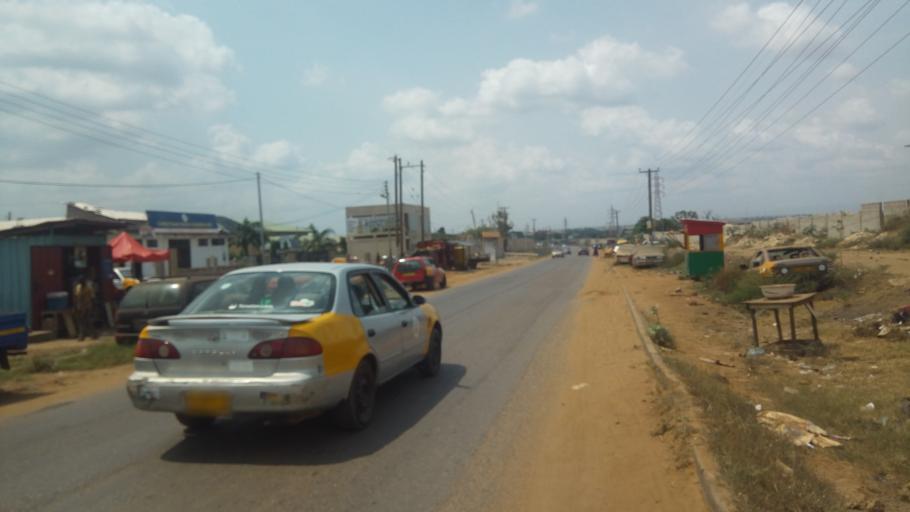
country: GH
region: Greater Accra
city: Tema
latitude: 5.7088
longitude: -0.0166
